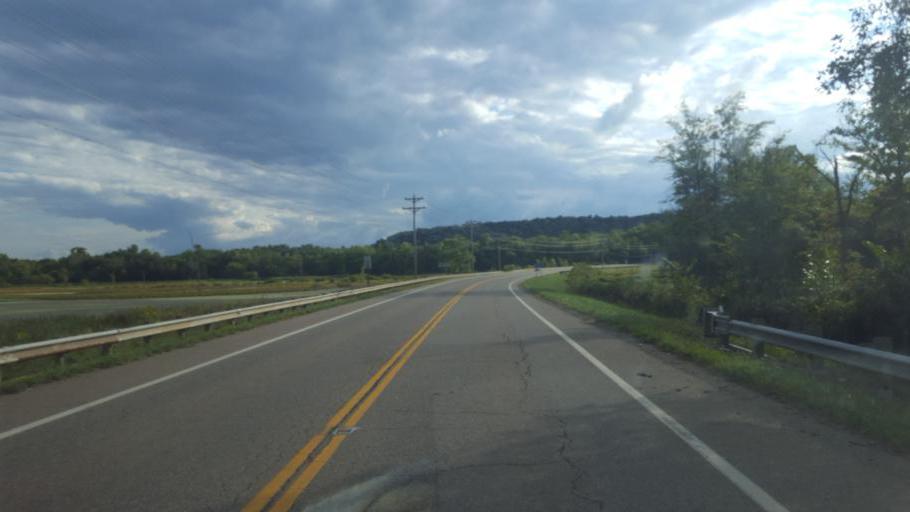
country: US
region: Ohio
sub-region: Holmes County
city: Millersburg
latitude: 40.4840
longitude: -81.9823
